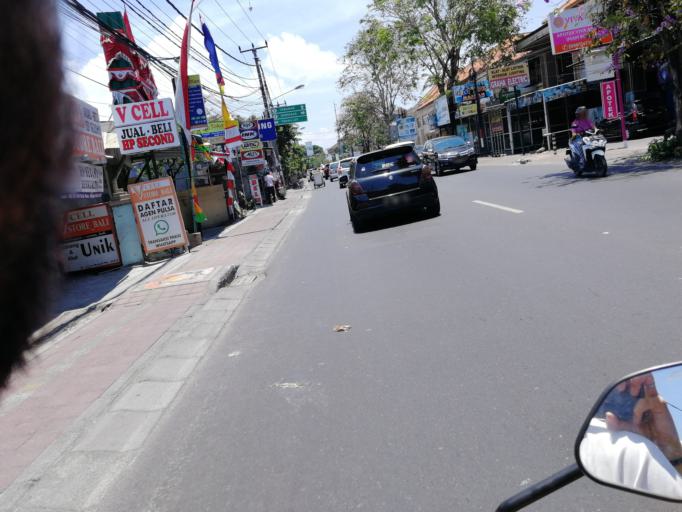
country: ID
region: Bali
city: Karyadharma
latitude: -8.6831
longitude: 115.1960
